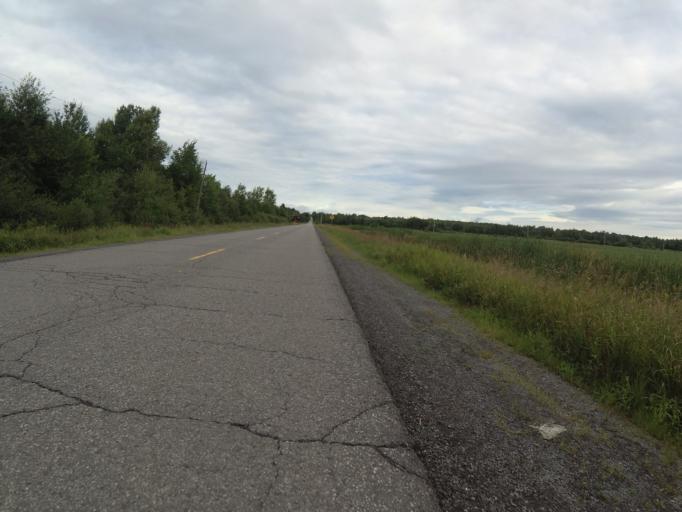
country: CA
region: Ontario
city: Clarence-Rockland
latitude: 45.4168
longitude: -75.2926
